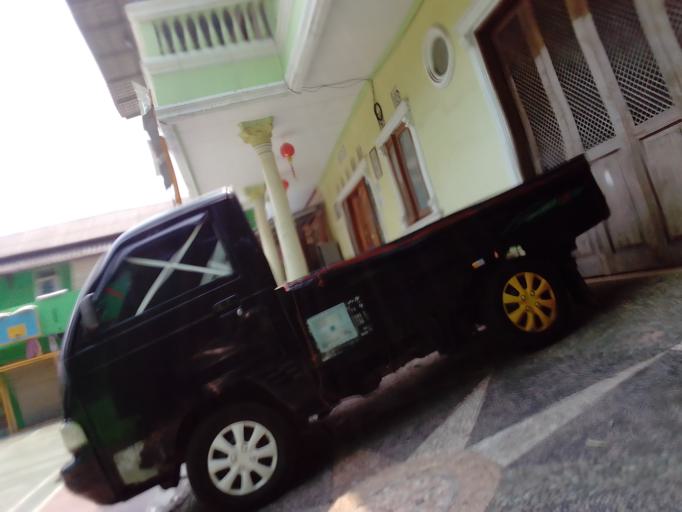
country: ID
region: Jakarta Raya
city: Jakarta
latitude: -6.2609
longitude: 106.7980
